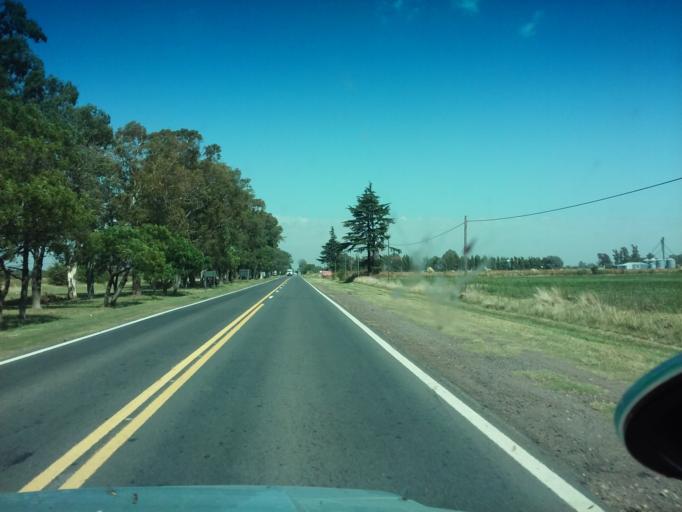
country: AR
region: Buenos Aires
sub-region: Partido de Nueve de Julio
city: Nueve de Julio
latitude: -35.4816
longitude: -60.8757
